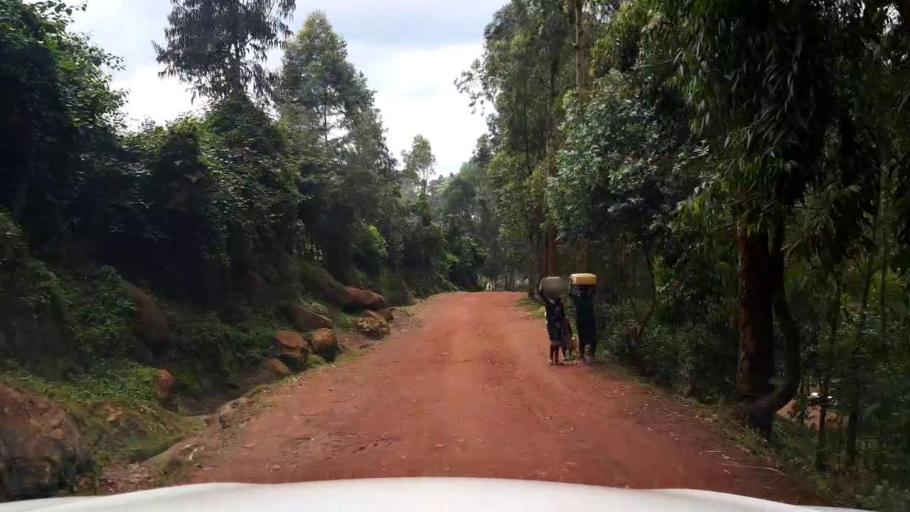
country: UG
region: Western Region
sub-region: Kisoro District
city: Kisoro
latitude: -1.4191
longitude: 29.8316
